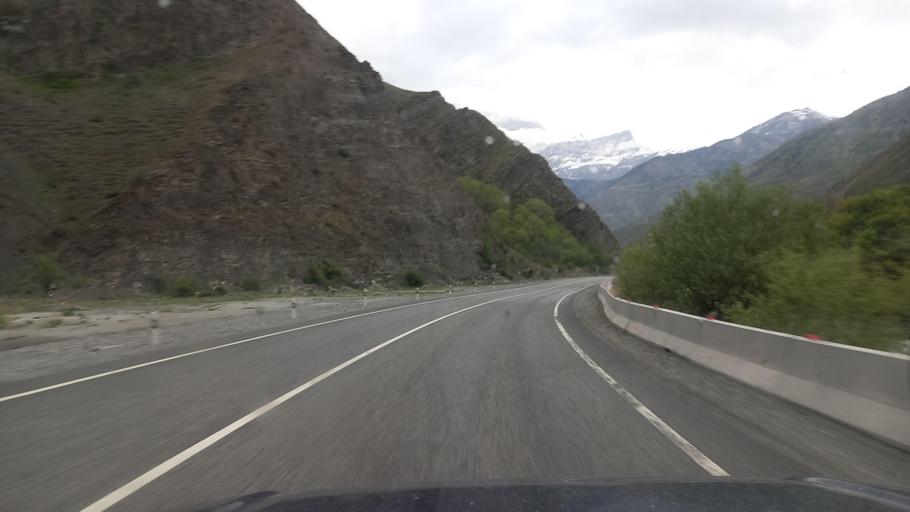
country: RU
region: North Ossetia
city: Mizur
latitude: 42.8577
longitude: 44.1074
